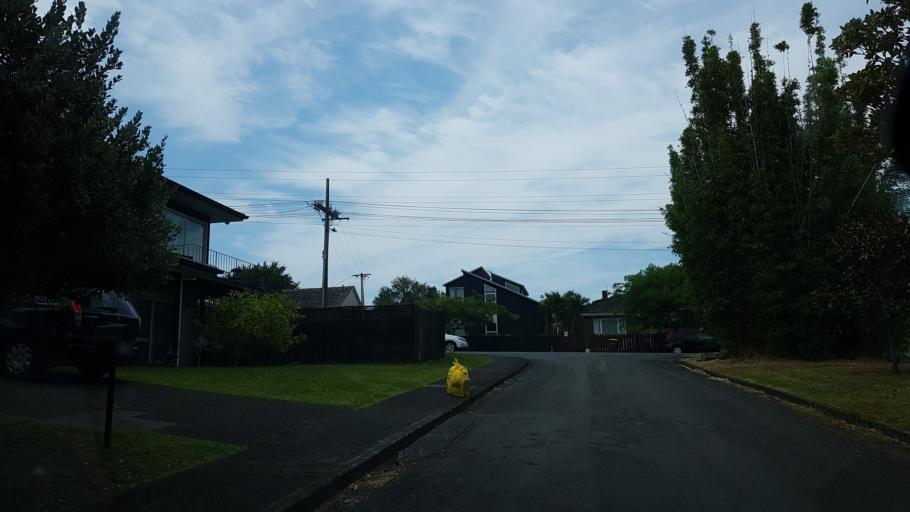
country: NZ
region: Auckland
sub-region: Auckland
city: North Shore
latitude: -36.8032
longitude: 174.7785
